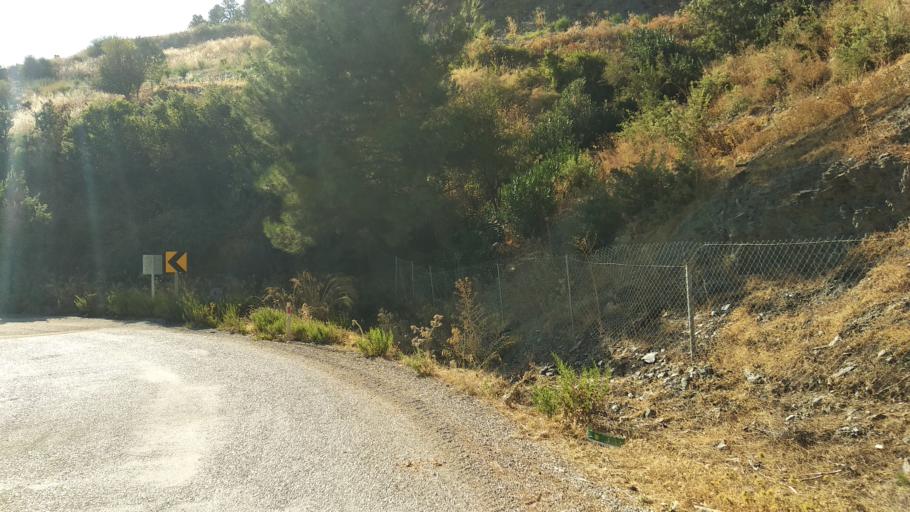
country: TR
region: Izmir
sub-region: Seferihisar
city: Seferhisar
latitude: 38.3227
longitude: 26.9367
